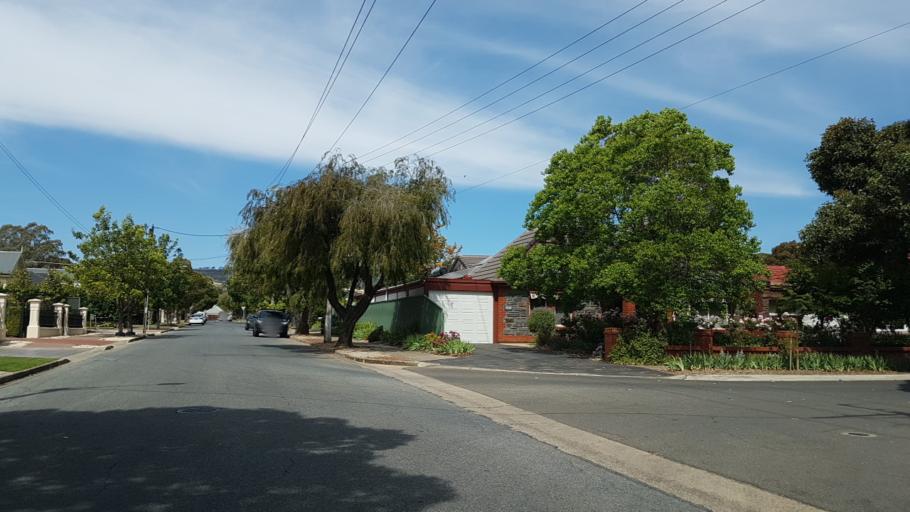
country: AU
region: South Australia
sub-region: Burnside
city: Kensington Gardens
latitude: -34.9104
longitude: 138.6647
